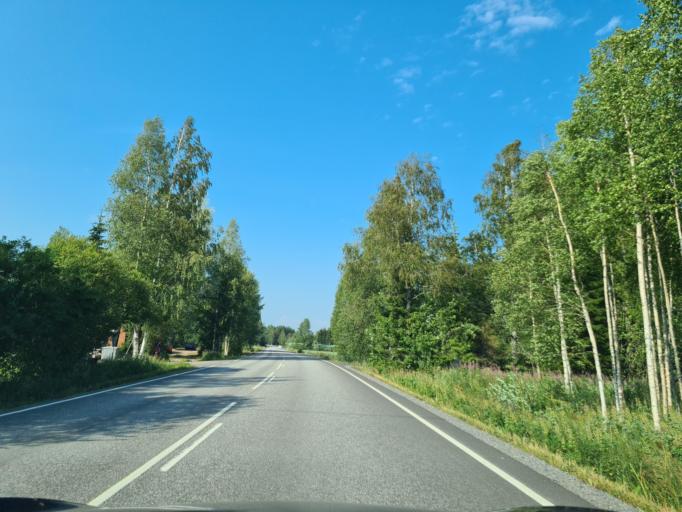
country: FI
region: Satakunta
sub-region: Pohjois-Satakunta
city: Kankaanpaeae
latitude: 61.9387
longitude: 22.5089
